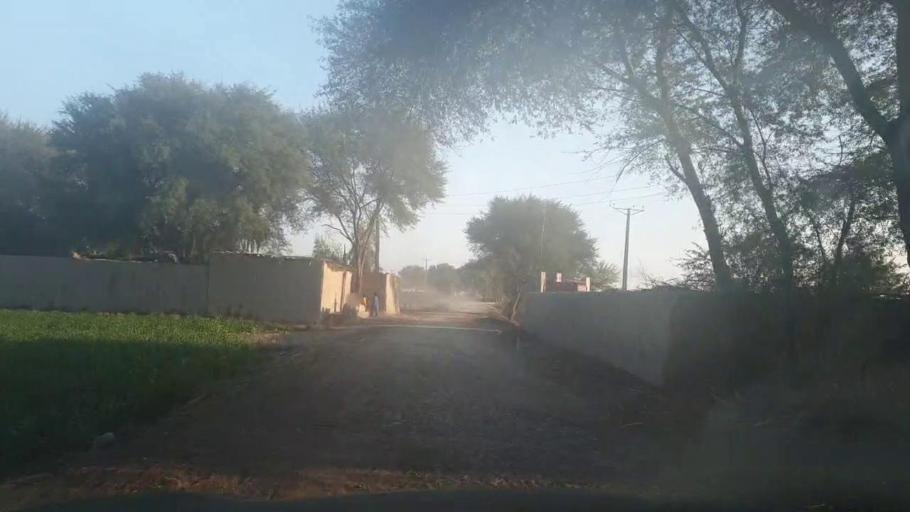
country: PK
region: Sindh
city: Mirpur Mathelo
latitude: 28.1717
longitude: 69.5773
